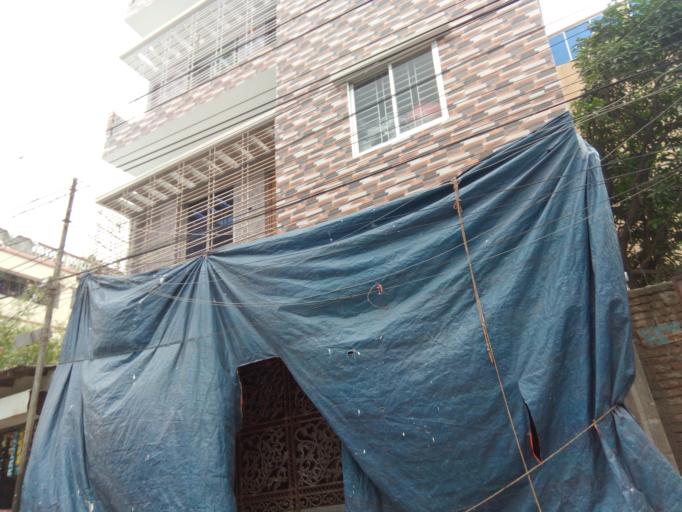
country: BD
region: Dhaka
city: Azimpur
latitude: 23.7185
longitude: 90.3664
